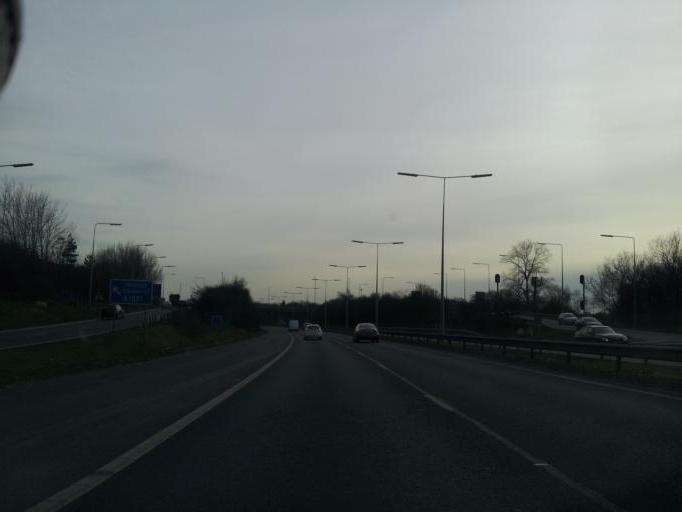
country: GB
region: England
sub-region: Hertfordshire
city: Hatfield
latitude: 51.7553
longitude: -0.2449
